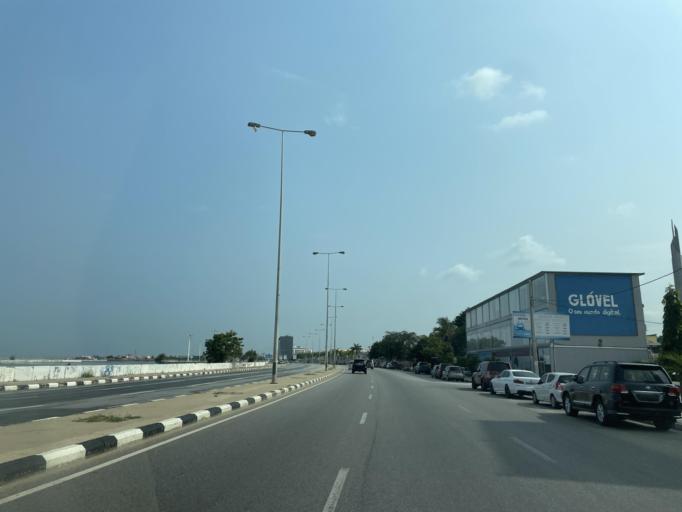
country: AO
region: Luanda
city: Luanda
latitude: -8.8265
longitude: 13.2149
